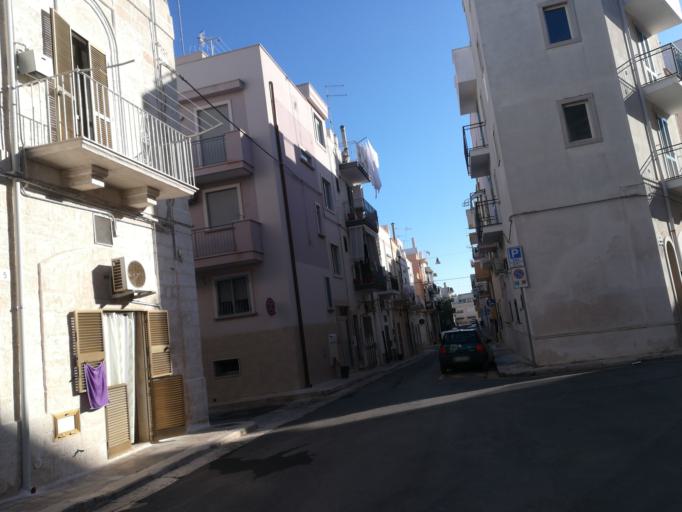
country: IT
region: Apulia
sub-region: Provincia di Bari
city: Polignano a Mare
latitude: 40.9942
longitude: 17.2232
